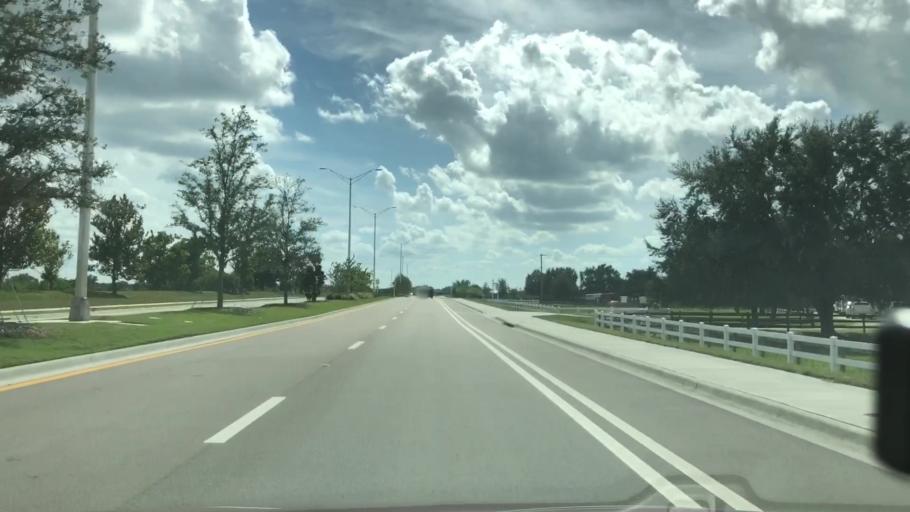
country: US
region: Florida
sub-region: Sarasota County
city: The Meadows
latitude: 27.3754
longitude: -82.3962
